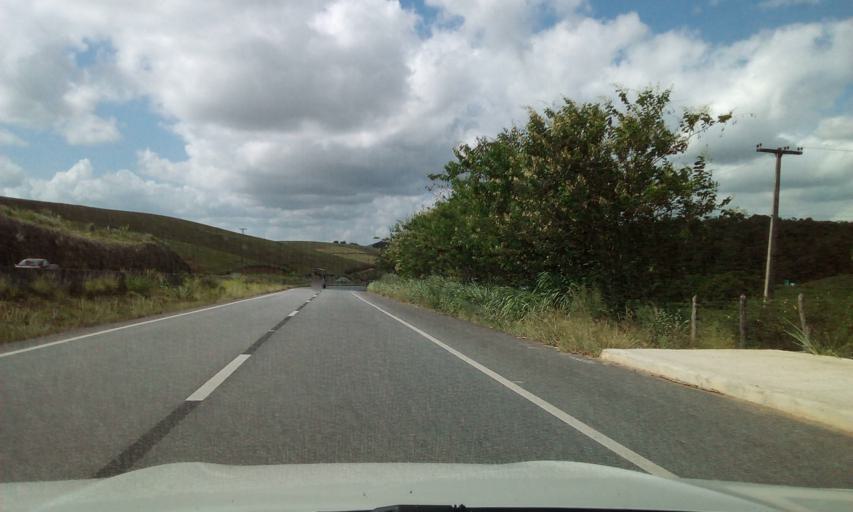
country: BR
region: Alagoas
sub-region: Messias
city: Messias
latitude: -9.3472
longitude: -35.8334
